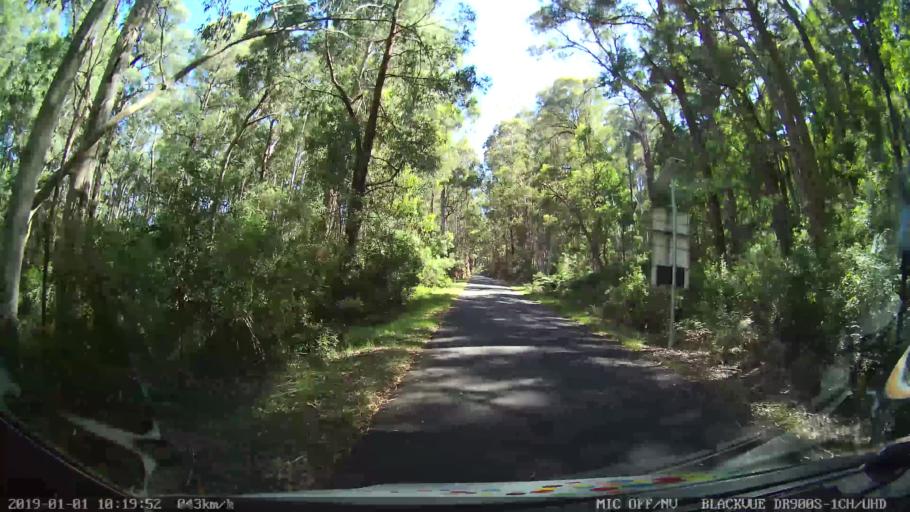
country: AU
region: New South Wales
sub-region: Snowy River
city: Jindabyne
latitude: -36.0817
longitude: 148.1865
